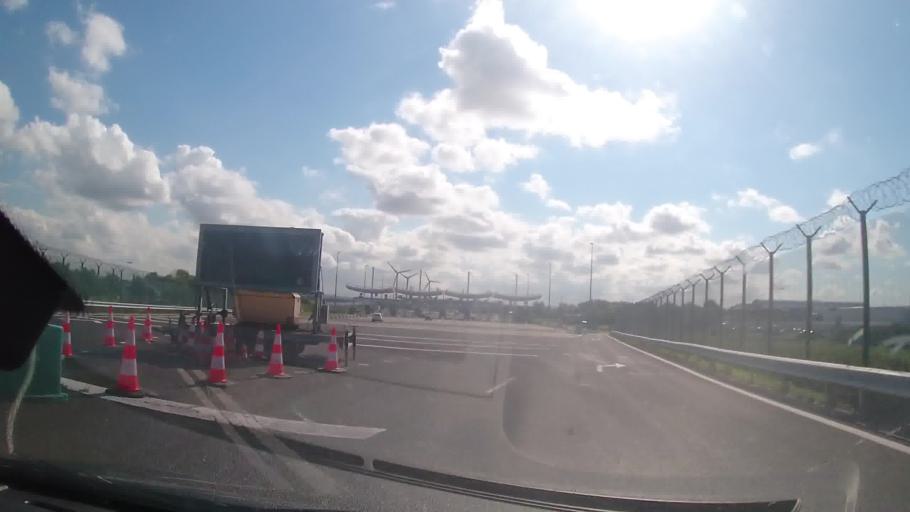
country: FR
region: Nord-Pas-de-Calais
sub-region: Departement du Pas-de-Calais
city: Coquelles
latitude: 50.9381
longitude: 1.8150
